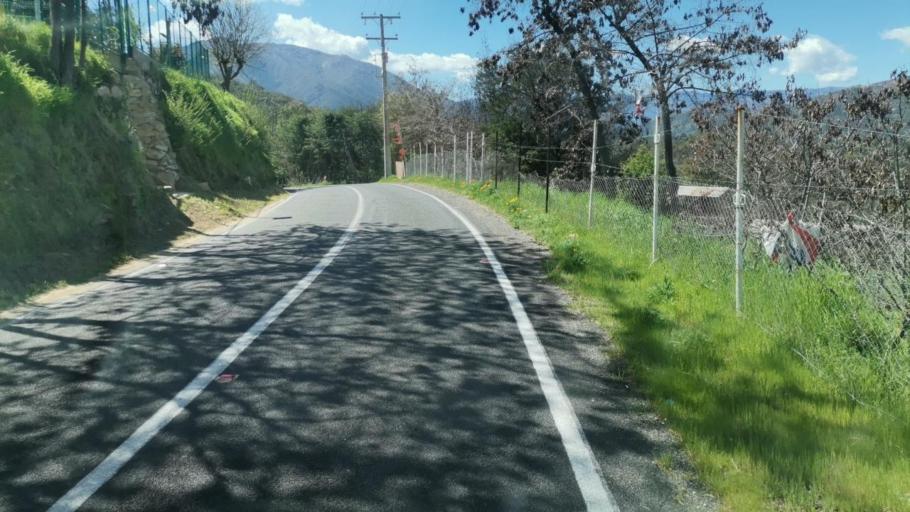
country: CL
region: Valparaiso
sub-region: Provincia de Marga Marga
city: Limache
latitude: -33.1908
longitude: -71.2019
